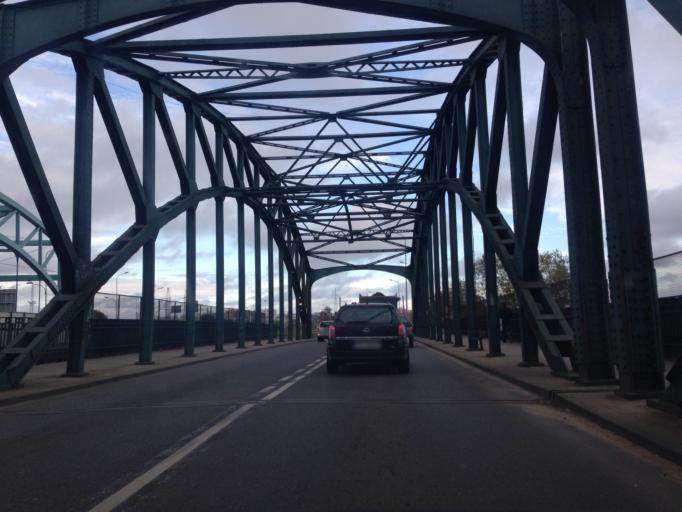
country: PL
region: Pomeranian Voivodeship
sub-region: Gdansk
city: Gdansk
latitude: 54.3841
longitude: 18.6003
